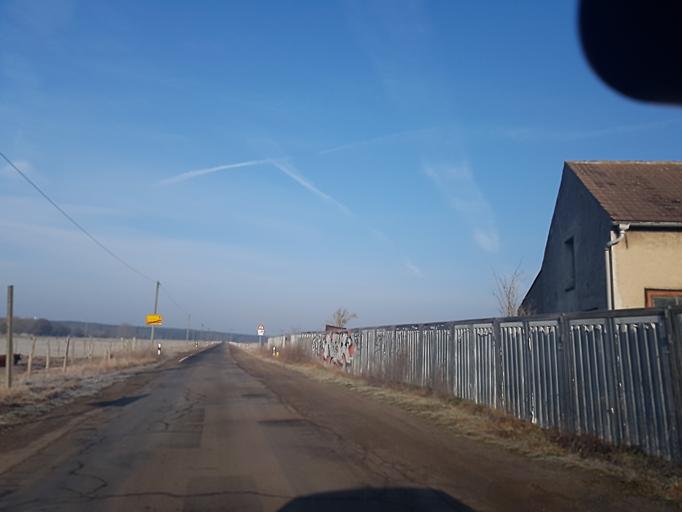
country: DE
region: Brandenburg
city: Wollin
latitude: 52.2498
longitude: 12.4820
